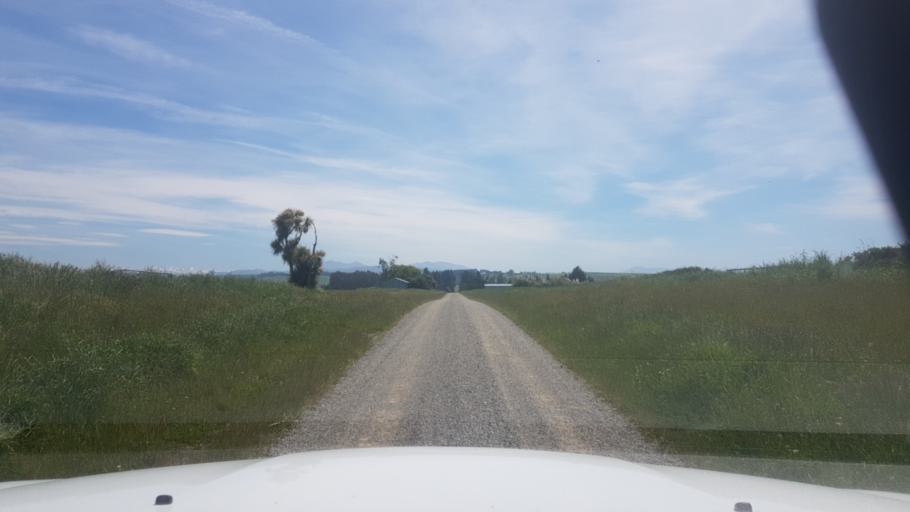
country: NZ
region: Canterbury
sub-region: Timaru District
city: Pleasant Point
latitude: -44.2284
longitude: 171.1655
